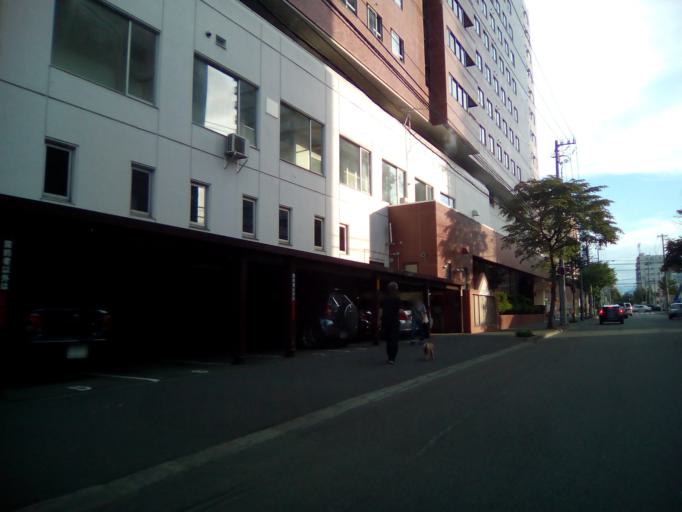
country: JP
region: Hokkaido
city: Sapporo
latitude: 43.0534
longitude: 141.3849
